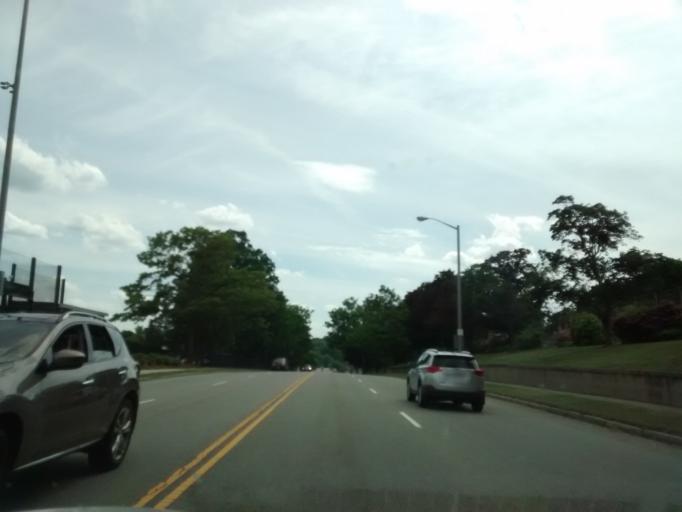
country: US
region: Massachusetts
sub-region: Worcester County
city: Worcester
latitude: 42.2755
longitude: -71.8114
